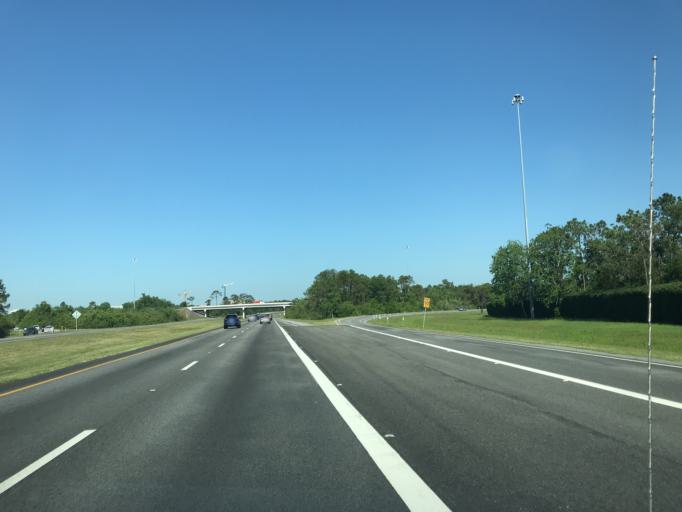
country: US
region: Florida
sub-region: Osceola County
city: Celebration
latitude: 28.3585
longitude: -81.5125
